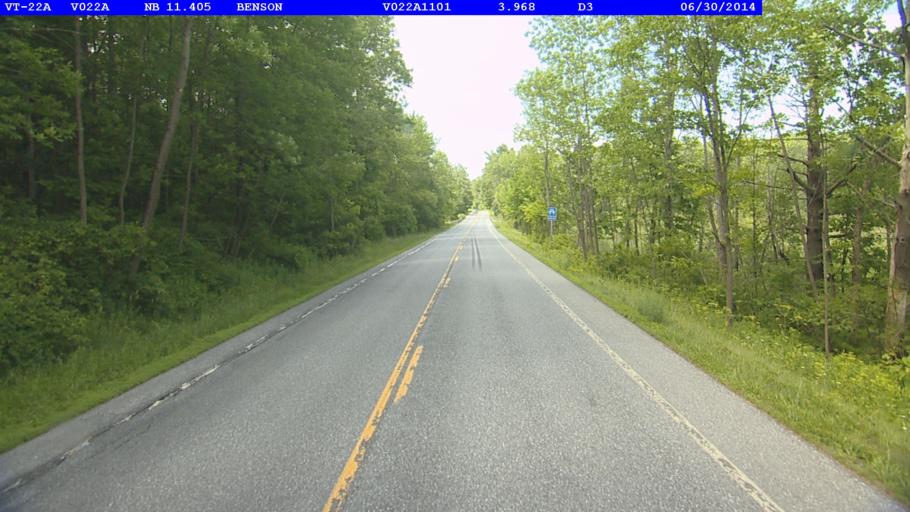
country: US
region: Vermont
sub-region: Rutland County
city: Fair Haven
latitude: 43.7252
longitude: -73.3013
